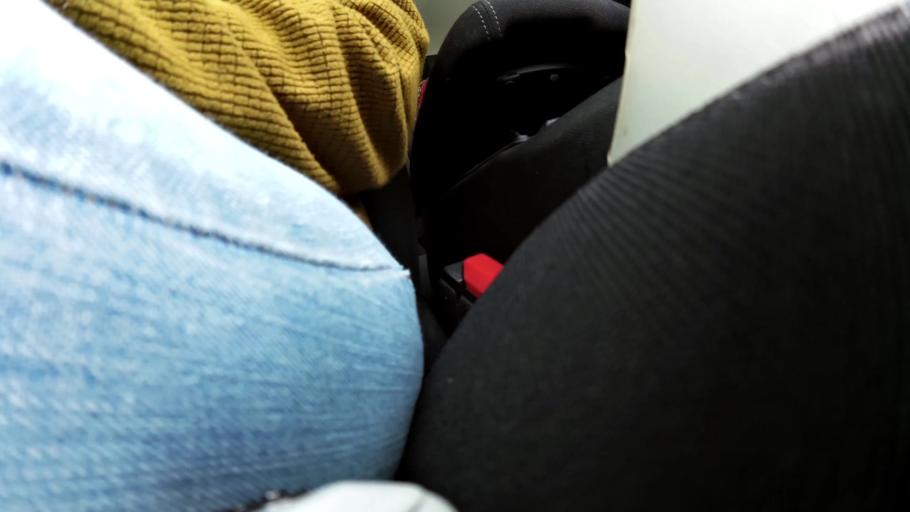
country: MA
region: Fes-Boulemane
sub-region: Fes
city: Fes
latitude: 34.0560
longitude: -4.9745
